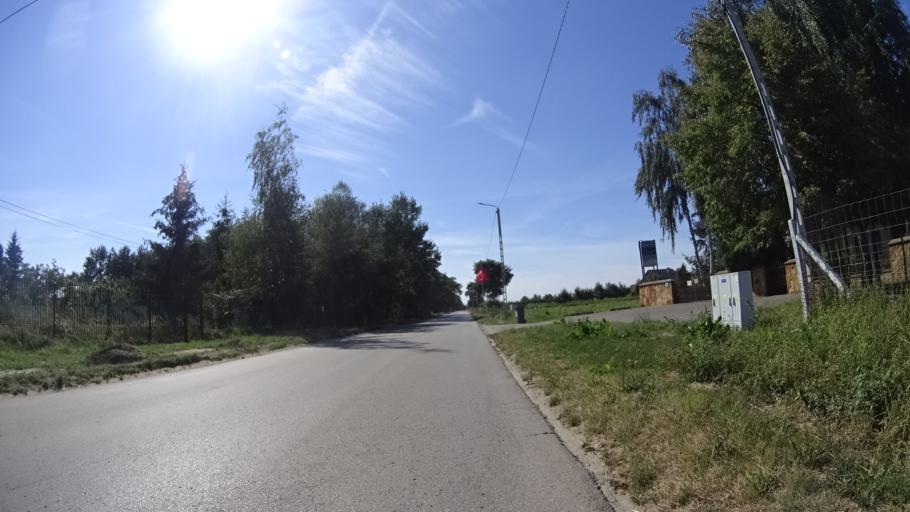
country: PL
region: Masovian Voivodeship
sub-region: Powiat bialobrzeski
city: Bialobrzegi
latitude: 51.6711
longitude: 20.9133
